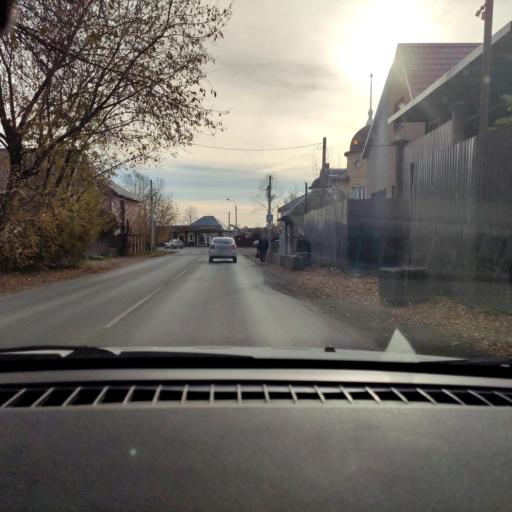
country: RU
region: Perm
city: Perm
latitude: 58.0488
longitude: 56.3365
